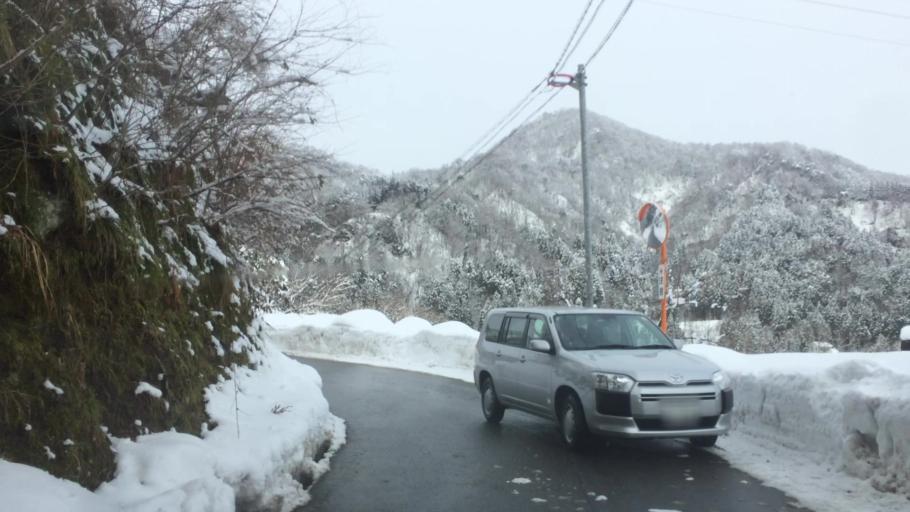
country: JP
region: Toyama
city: Kamiichi
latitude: 36.5705
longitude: 137.3746
